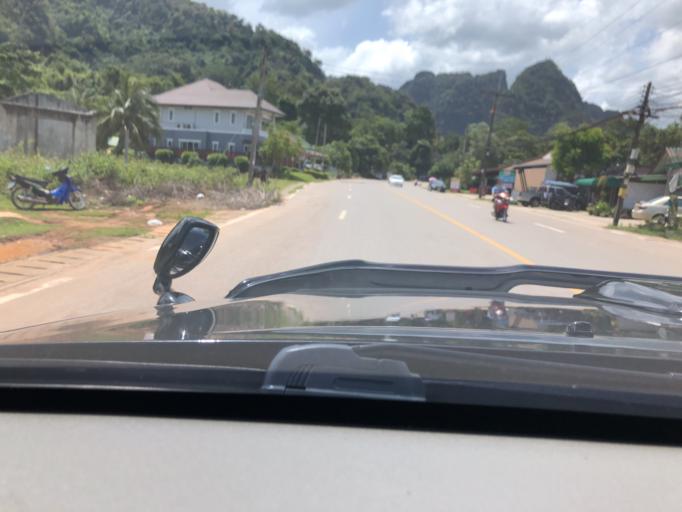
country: TH
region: Krabi
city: Krabi
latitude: 8.1138
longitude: 98.9232
